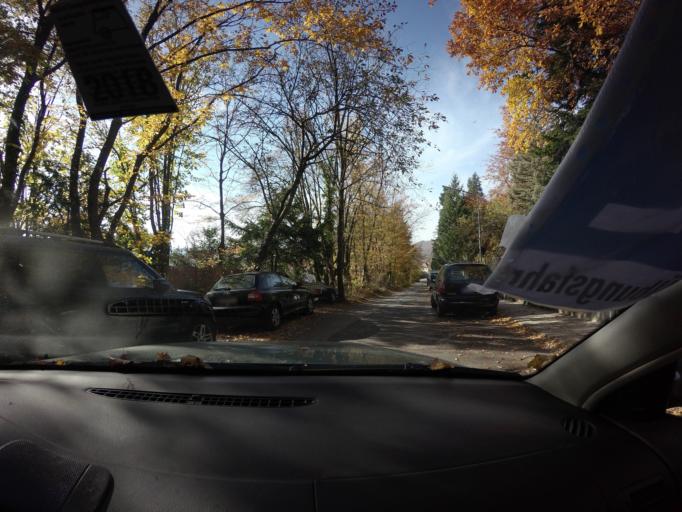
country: AT
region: Lower Austria
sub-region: Politischer Bezirk Wien-Umgebung
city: Purkersdorf
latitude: 48.2122
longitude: 16.2193
